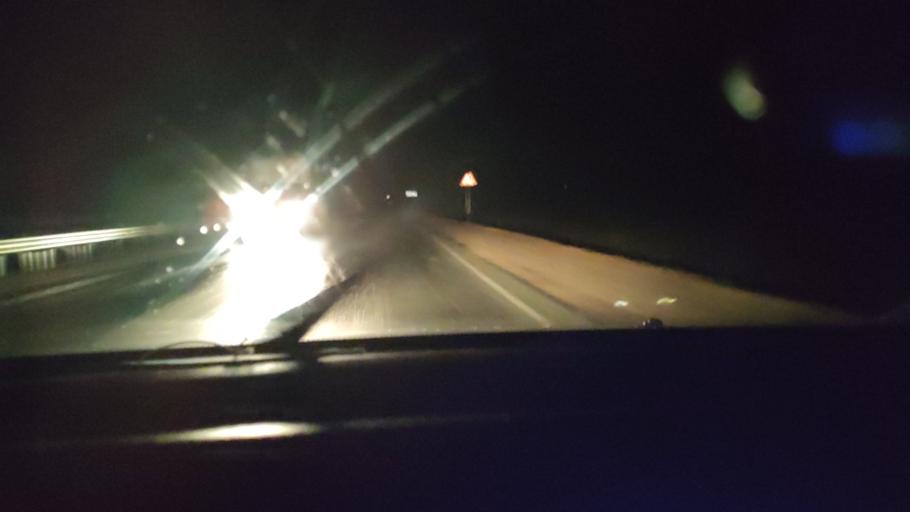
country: RU
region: Udmurtiya
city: Votkinsk
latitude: 57.3629
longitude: 54.4209
